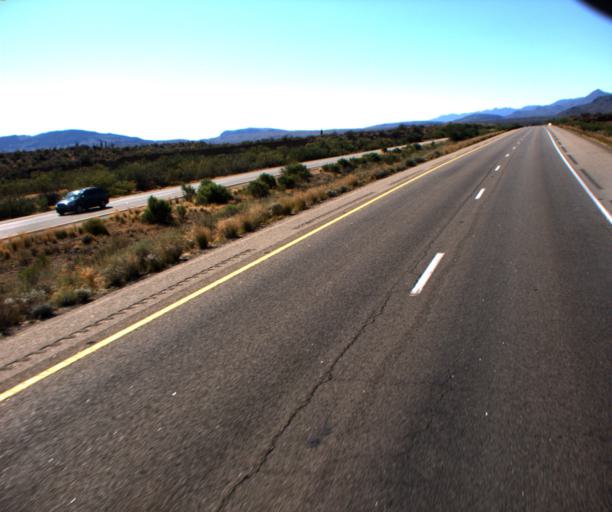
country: US
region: Arizona
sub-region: Yavapai County
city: Bagdad
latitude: 34.6585
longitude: -113.5772
